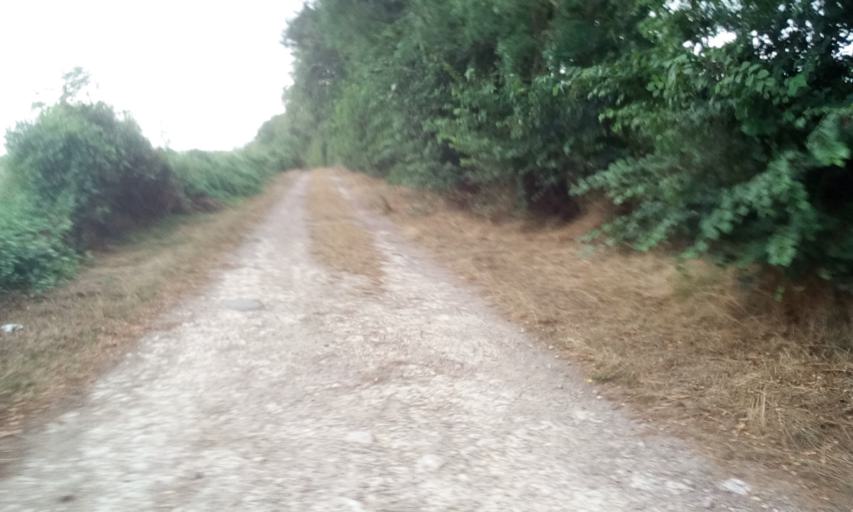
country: FR
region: Lower Normandy
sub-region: Departement du Calvados
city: Troarn
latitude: 49.1840
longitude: -0.1995
